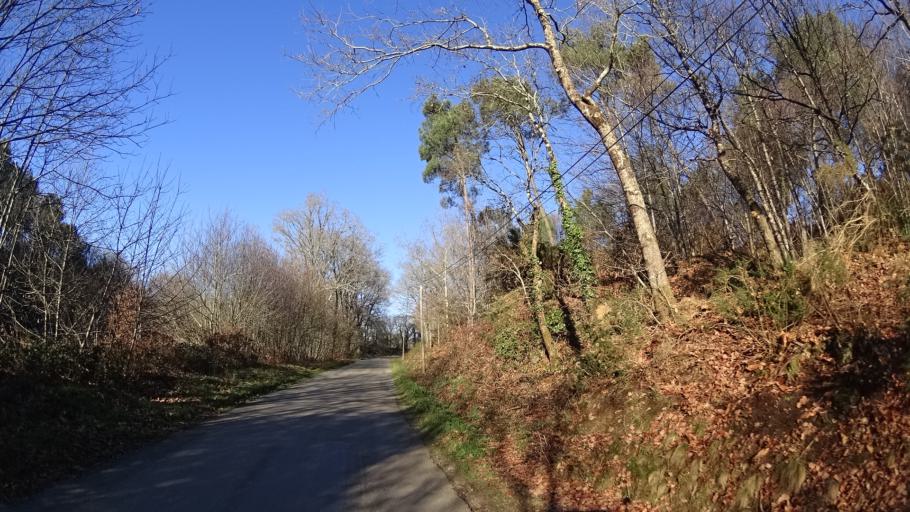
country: FR
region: Brittany
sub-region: Departement du Morbihan
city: Allaire
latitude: 47.6219
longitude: -2.1897
